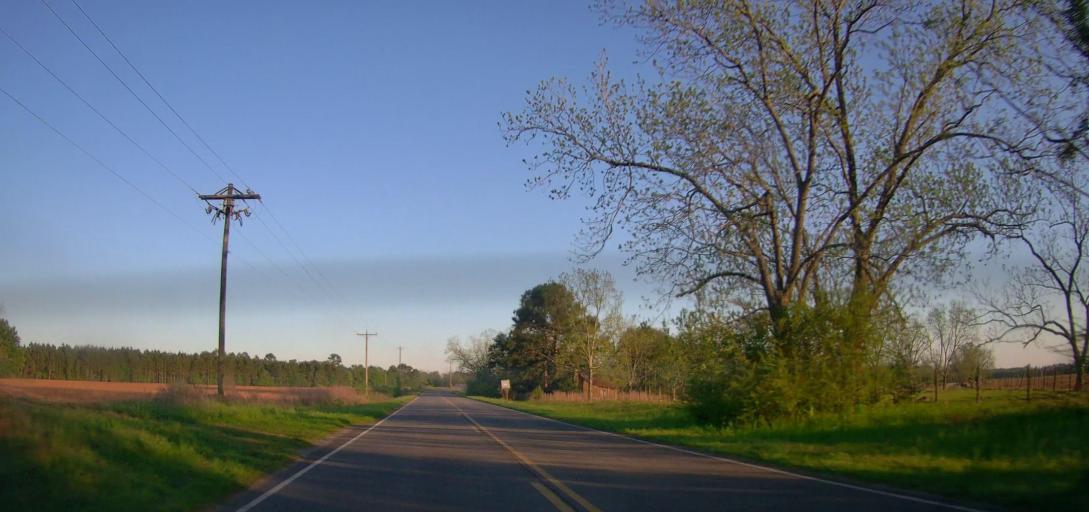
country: US
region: Georgia
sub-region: Irwin County
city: Ocilla
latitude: 31.6097
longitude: -83.2608
